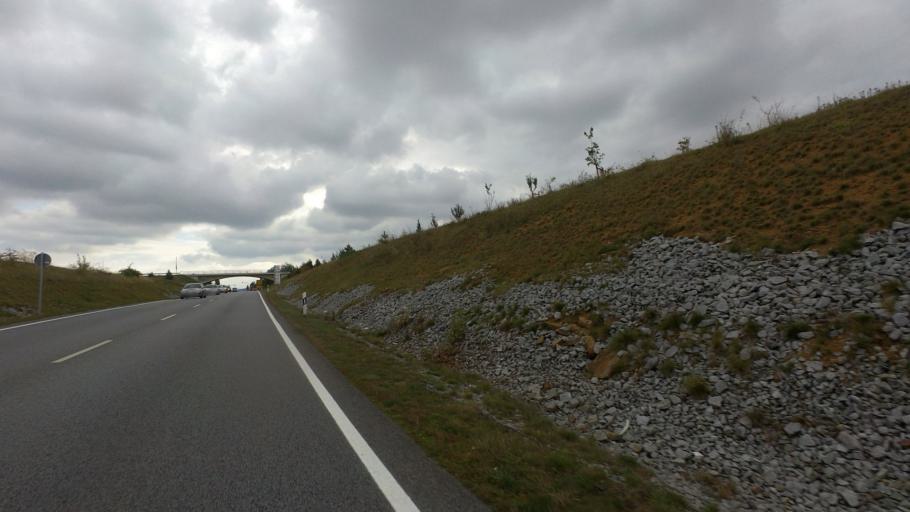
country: DE
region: Saxony
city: Bautzen
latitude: 51.1839
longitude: 14.4105
